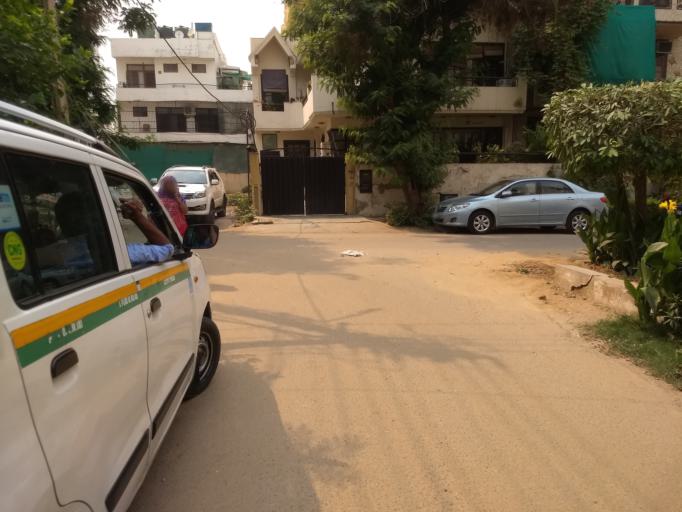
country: IN
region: Haryana
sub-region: Gurgaon
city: Gurgaon
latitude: 28.4886
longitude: 77.0896
